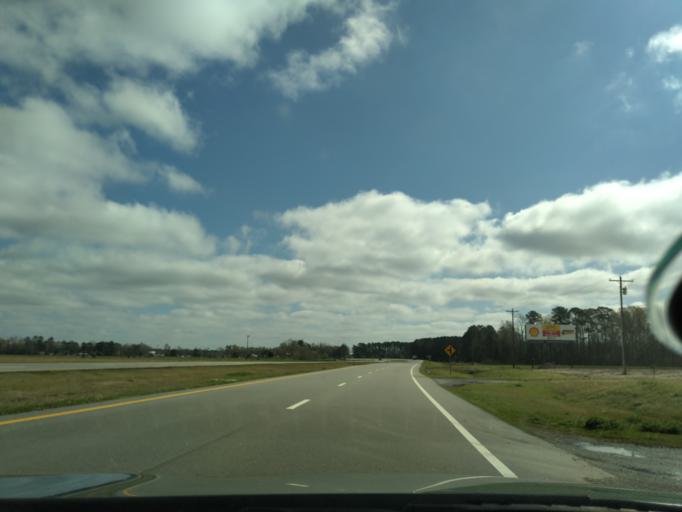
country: US
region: North Carolina
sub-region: Chowan County
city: Edenton
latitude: 36.0970
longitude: -76.5411
